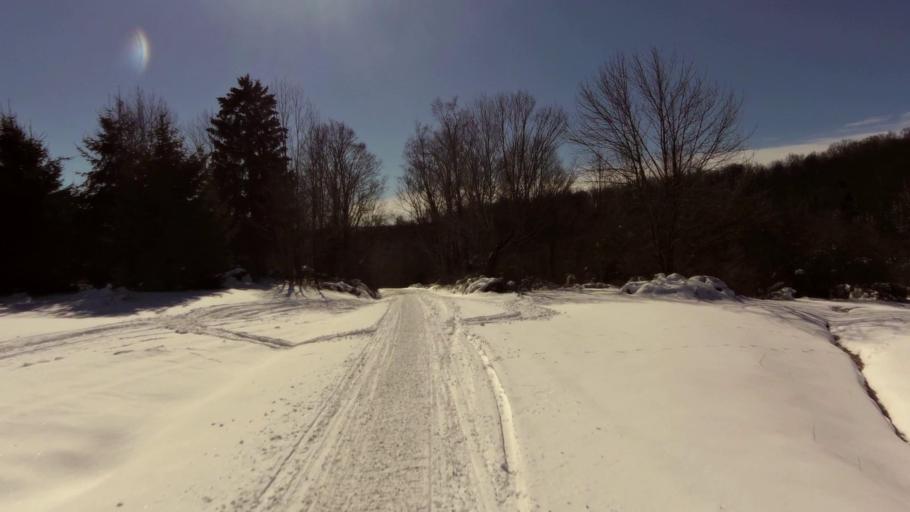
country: US
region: New York
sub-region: Allegany County
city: Cuba
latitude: 42.2848
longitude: -78.2355
